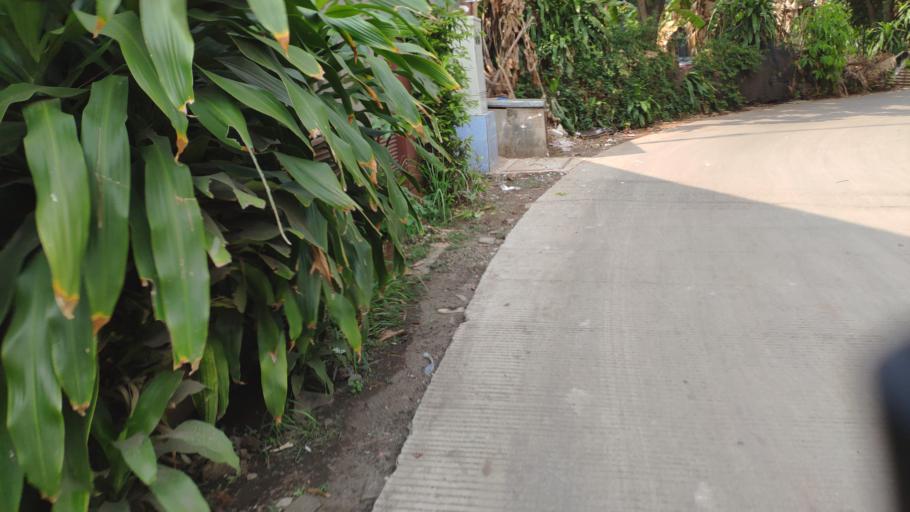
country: ID
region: West Java
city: Depok
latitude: -6.3119
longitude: 106.8311
